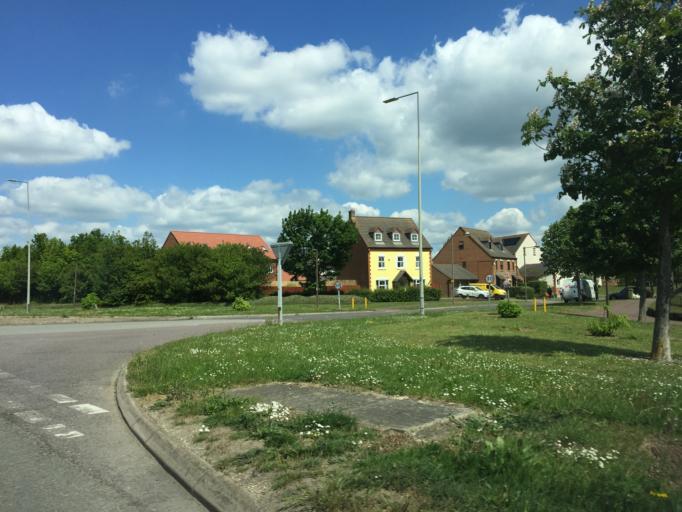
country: GB
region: England
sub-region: Milton Keynes
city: Simpson
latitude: 52.0344
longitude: -0.7085
